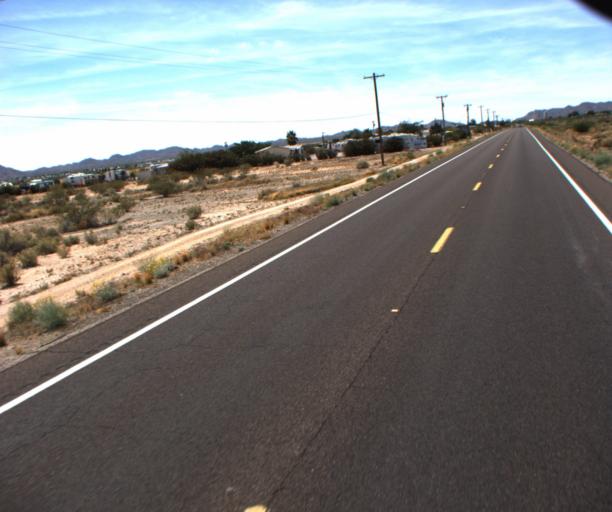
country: US
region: Arizona
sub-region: La Paz County
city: Salome
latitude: 33.7886
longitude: -113.6023
